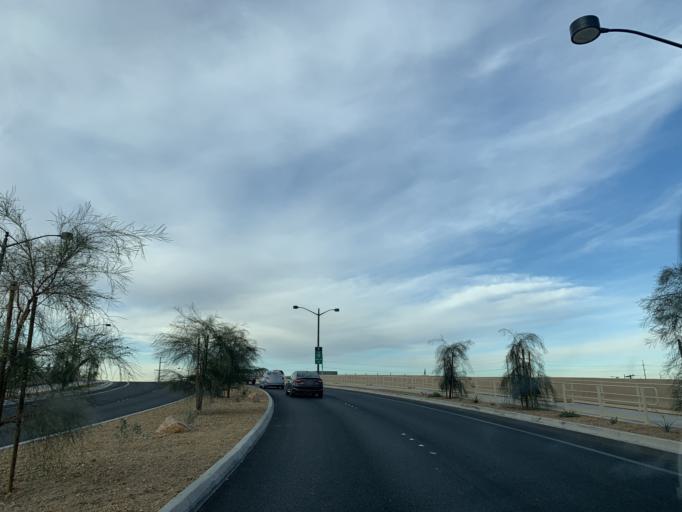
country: US
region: Nevada
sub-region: Clark County
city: Las Vegas
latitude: 36.1548
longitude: -115.1582
